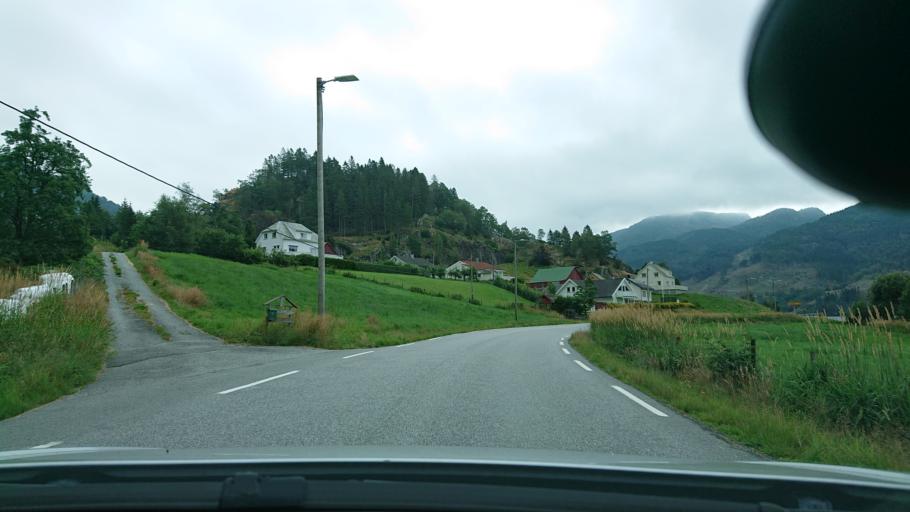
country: NO
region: Rogaland
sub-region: Hjelmeland
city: Hjelmelandsvagen
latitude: 59.2339
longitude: 6.1888
